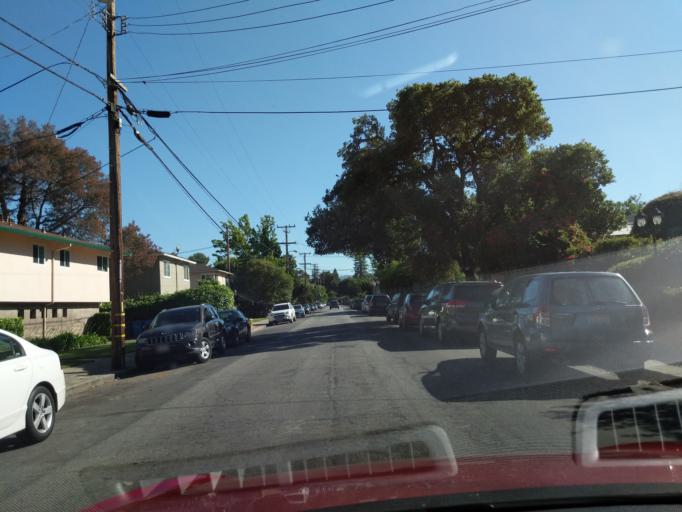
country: US
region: California
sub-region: San Mateo County
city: Menlo Park
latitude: 37.4495
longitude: -122.1818
